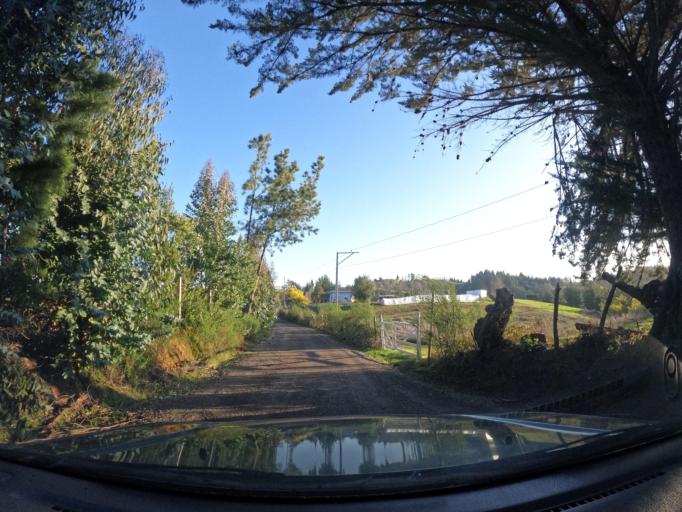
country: CL
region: Biobio
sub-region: Provincia de Concepcion
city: Chiguayante
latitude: -37.0133
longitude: -72.8473
